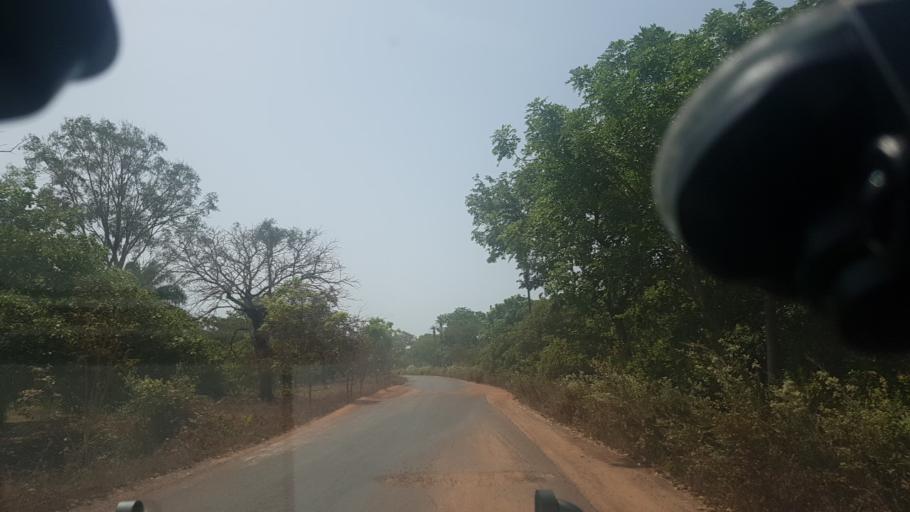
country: GW
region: Cacheu
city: Cacheu
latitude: 12.4098
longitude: -16.0301
